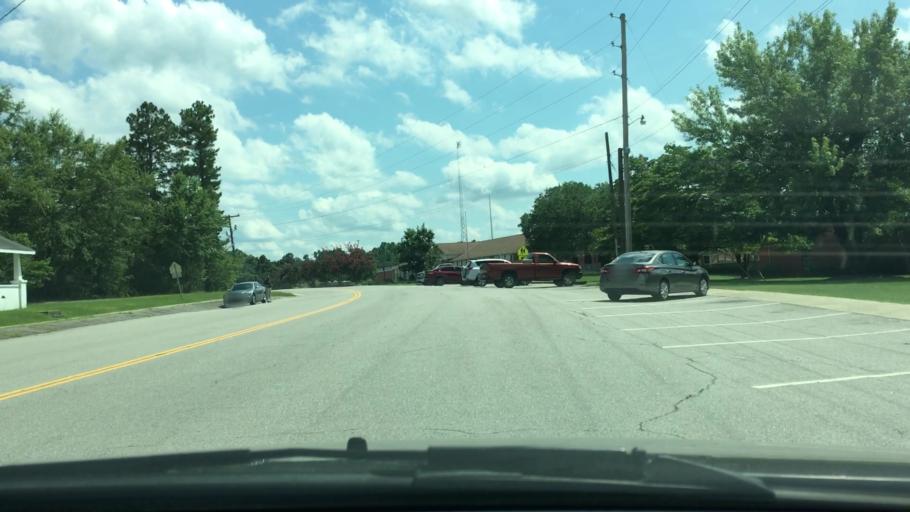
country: US
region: South Carolina
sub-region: Barnwell County
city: Williston
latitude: 33.6479
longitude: -81.3639
